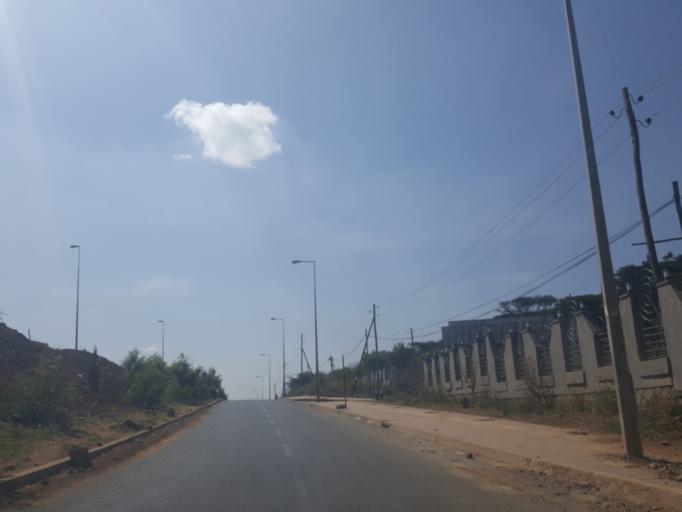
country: ET
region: Adis Abeba
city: Addis Ababa
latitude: 9.0661
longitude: 38.7147
